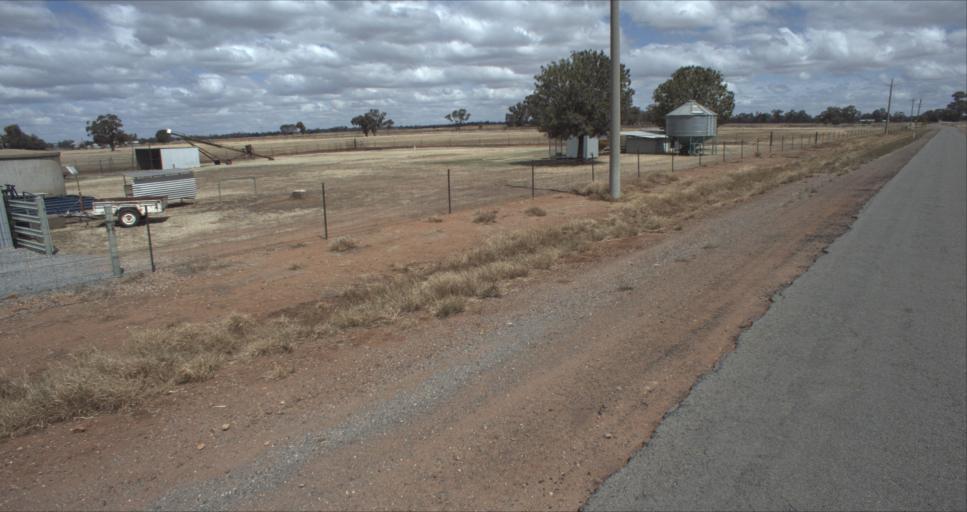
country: AU
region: New South Wales
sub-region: Leeton
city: Leeton
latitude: -34.5880
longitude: 146.3711
